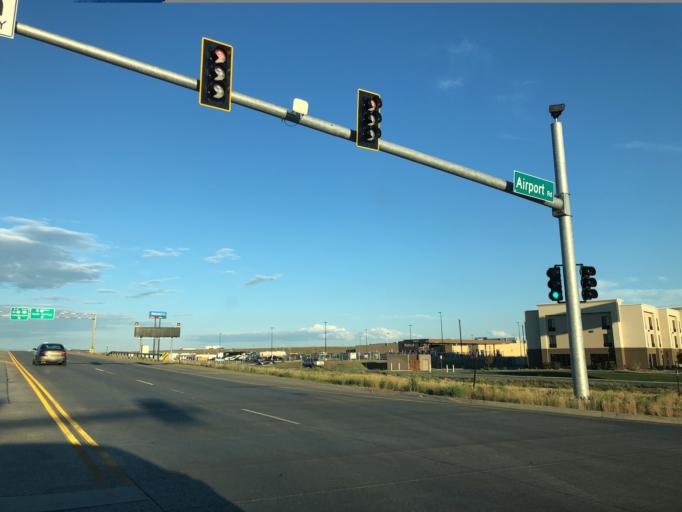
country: US
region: Wyoming
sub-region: Carbon County
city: Rawlins
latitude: 41.7920
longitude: -107.2088
